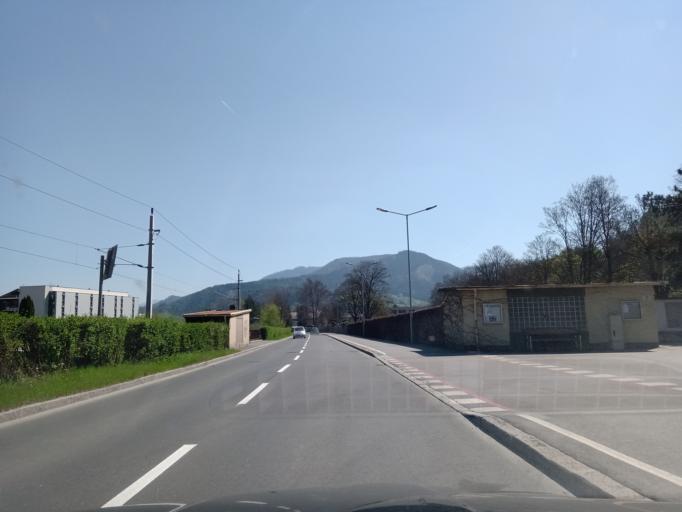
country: AT
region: Styria
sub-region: Politischer Bezirk Leoben
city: Leoben
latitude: 47.3744
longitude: 15.0758
